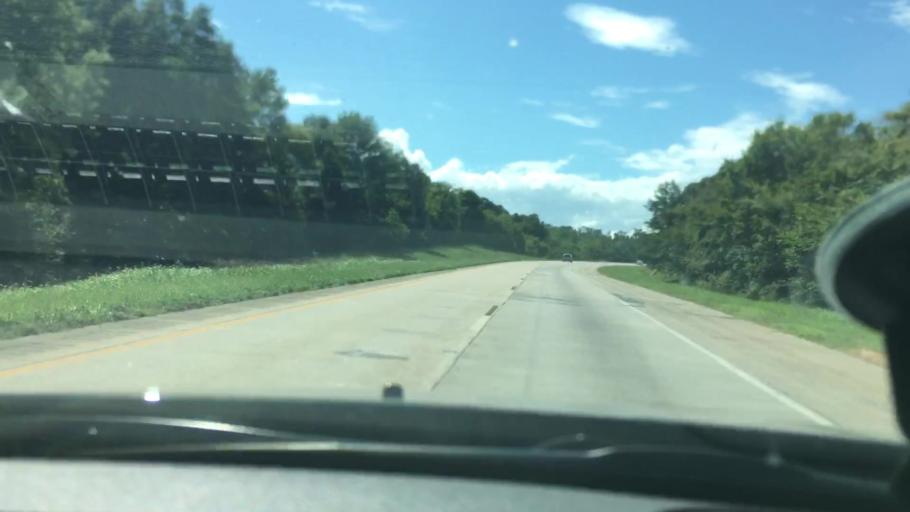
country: US
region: Oklahoma
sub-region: Sequoyah County
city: Vian
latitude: 35.4901
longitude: -94.9915
